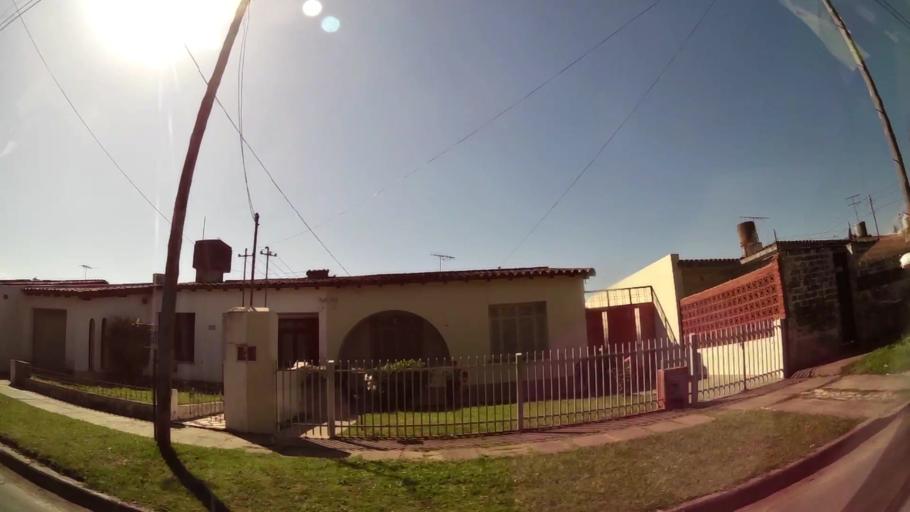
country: AR
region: Buenos Aires
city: Hurlingham
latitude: -34.4985
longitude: -58.6894
